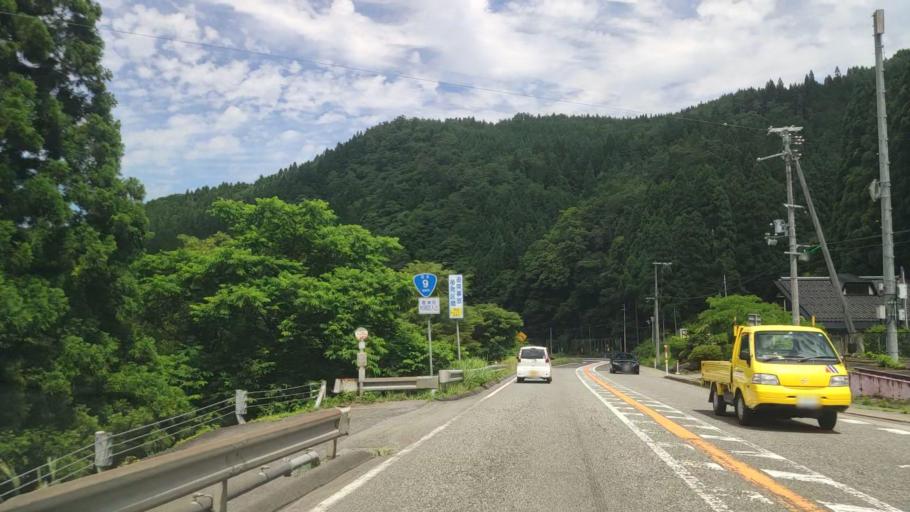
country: JP
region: Hyogo
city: Toyooka
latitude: 35.4869
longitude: 134.5754
